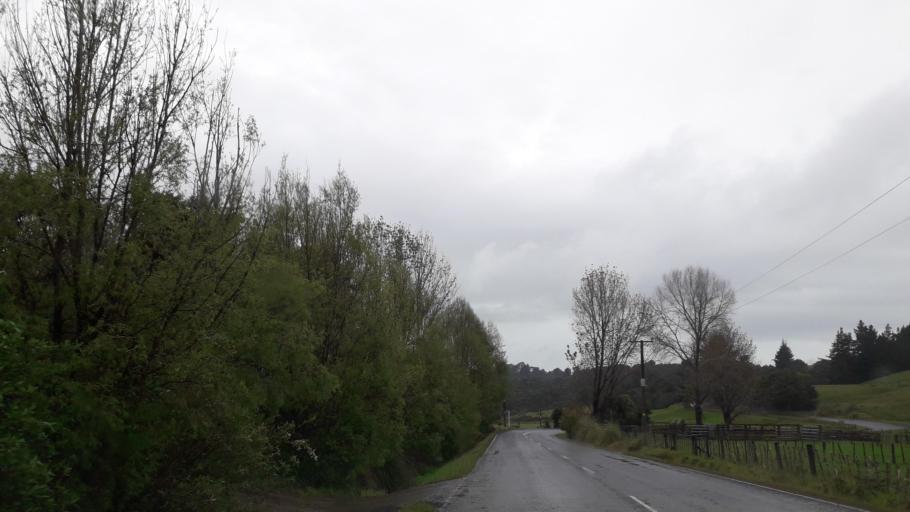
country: NZ
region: Northland
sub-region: Far North District
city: Kaitaia
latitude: -35.3607
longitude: 173.4812
